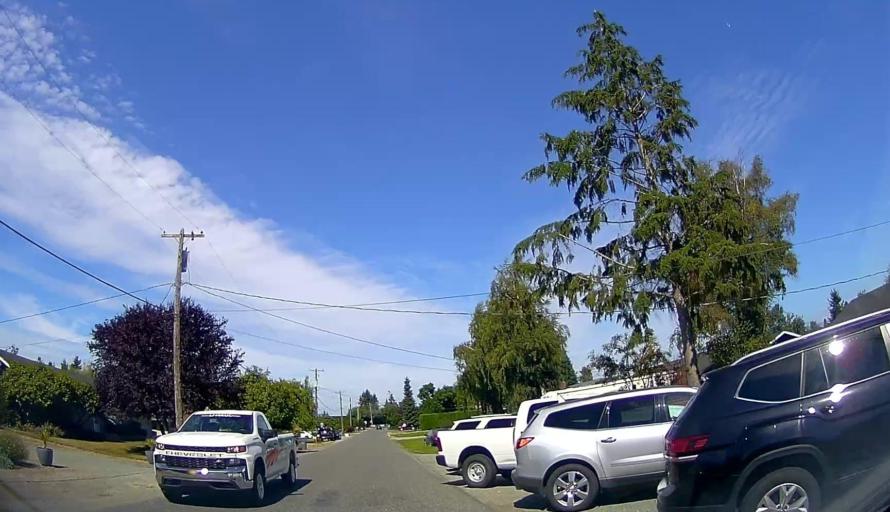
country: US
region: Washington
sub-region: Skagit County
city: Mount Vernon
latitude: 48.4254
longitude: -122.3618
